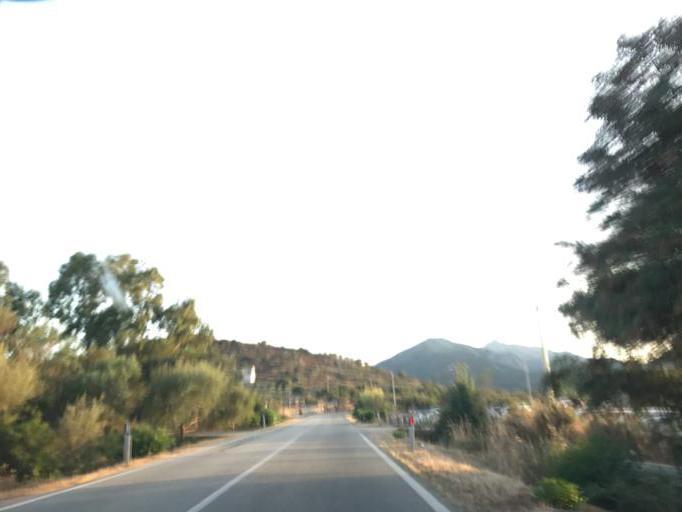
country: IT
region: Sardinia
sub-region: Provincia di Olbia-Tempio
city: San Teodoro
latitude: 40.7622
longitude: 9.6610
